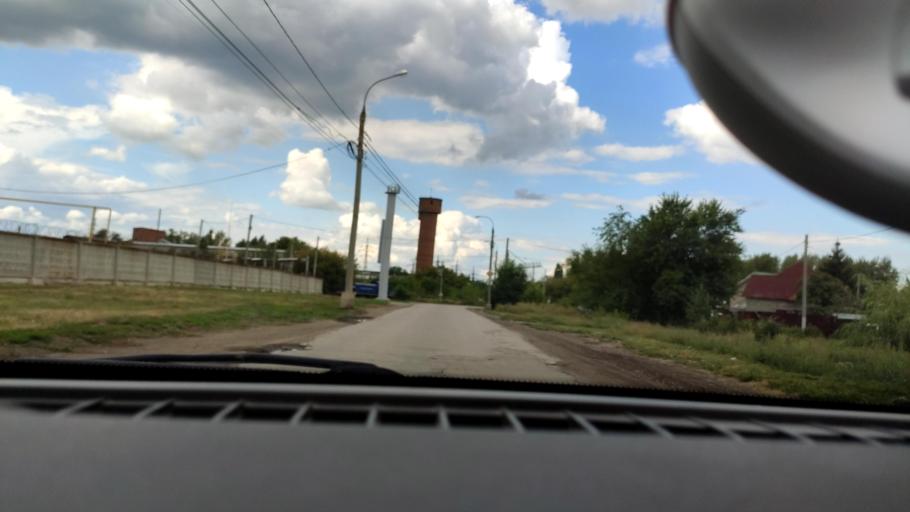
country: RU
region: Samara
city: Novokuybyshevsk
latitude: 53.1078
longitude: 50.0418
